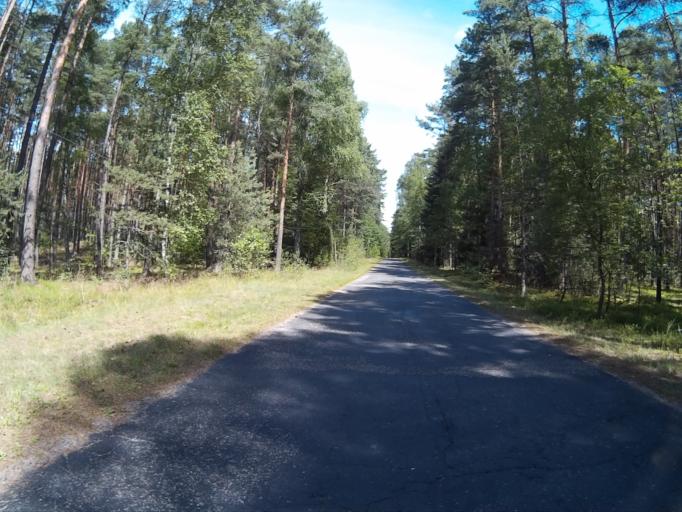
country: PL
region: Pomeranian Voivodeship
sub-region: Powiat chojnicki
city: Czersk
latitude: 53.6963
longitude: 17.9948
